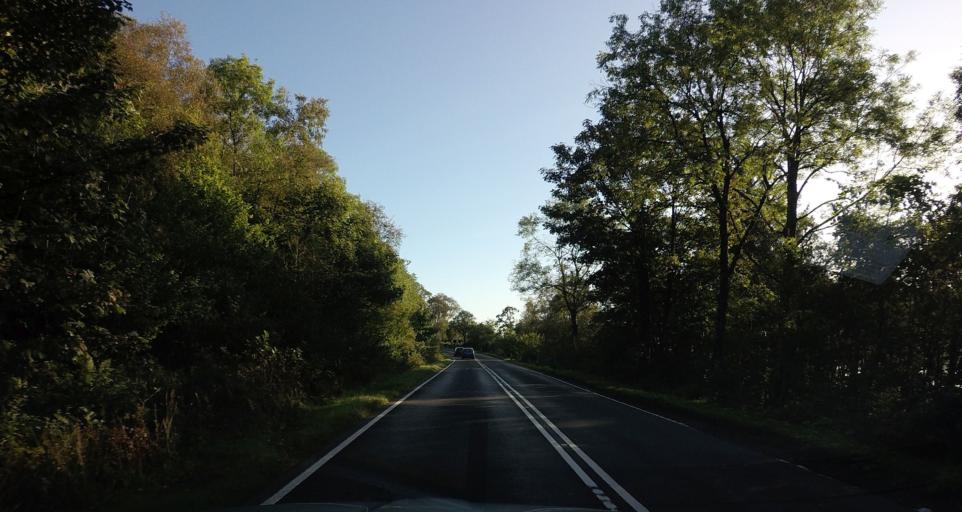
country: GB
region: Scotland
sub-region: Highland
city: Fort William
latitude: 56.7243
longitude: -5.2320
